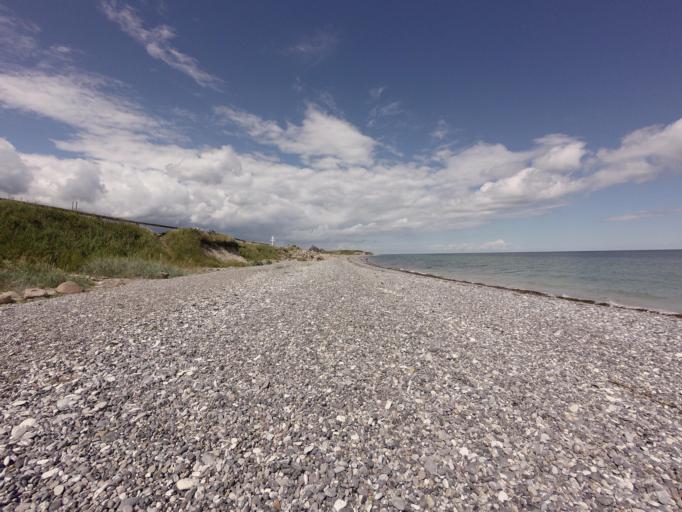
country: DK
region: Central Jutland
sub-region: Norddjurs Kommune
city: Grenaa
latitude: 56.5191
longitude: 10.8566
